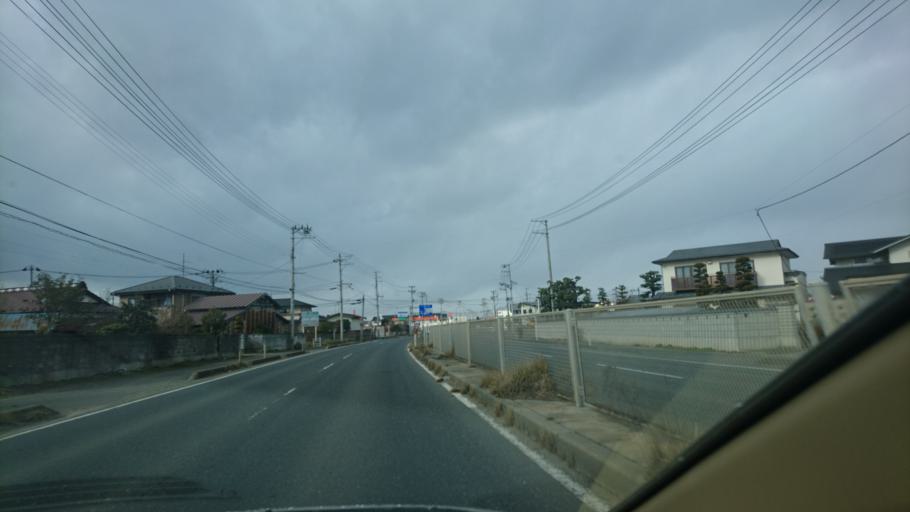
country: JP
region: Miyagi
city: Tomiya
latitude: 38.4382
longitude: 140.9071
